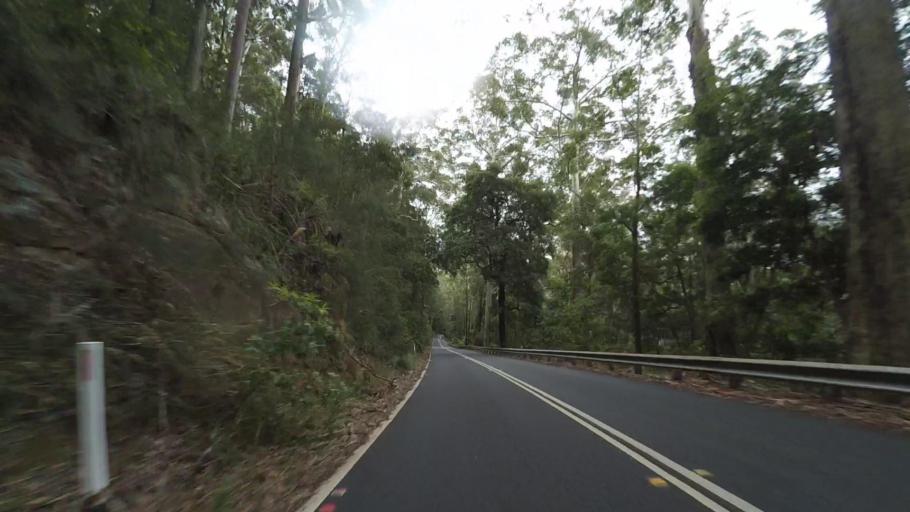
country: AU
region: New South Wales
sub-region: Wollongong
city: Helensburgh
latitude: -34.1533
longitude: 151.0327
